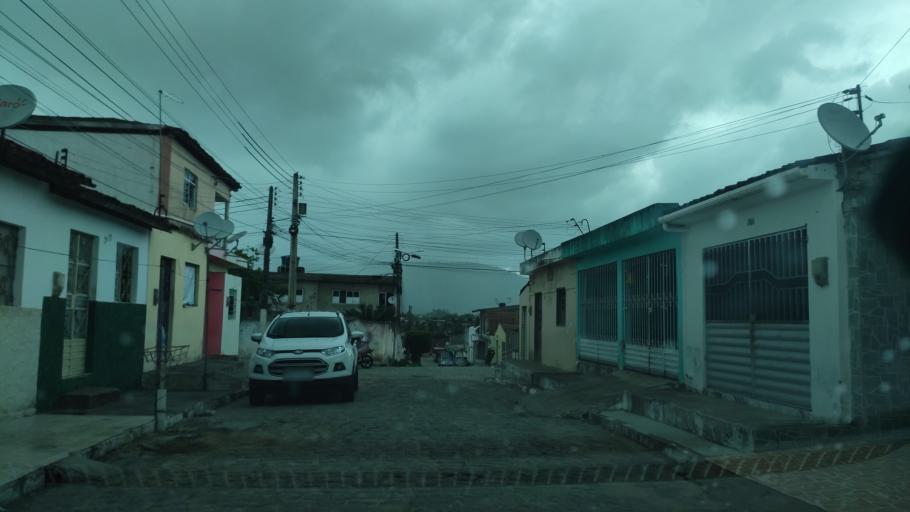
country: BR
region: Alagoas
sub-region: Uniao Dos Palmares
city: Uniao dos Palmares
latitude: -9.1601
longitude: -36.0260
